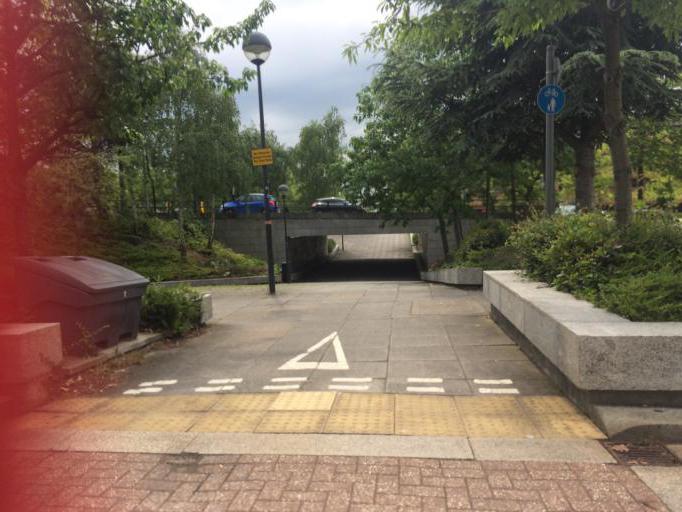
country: GB
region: England
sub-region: Milton Keynes
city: Milton Keynes
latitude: 52.0405
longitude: -0.7664
